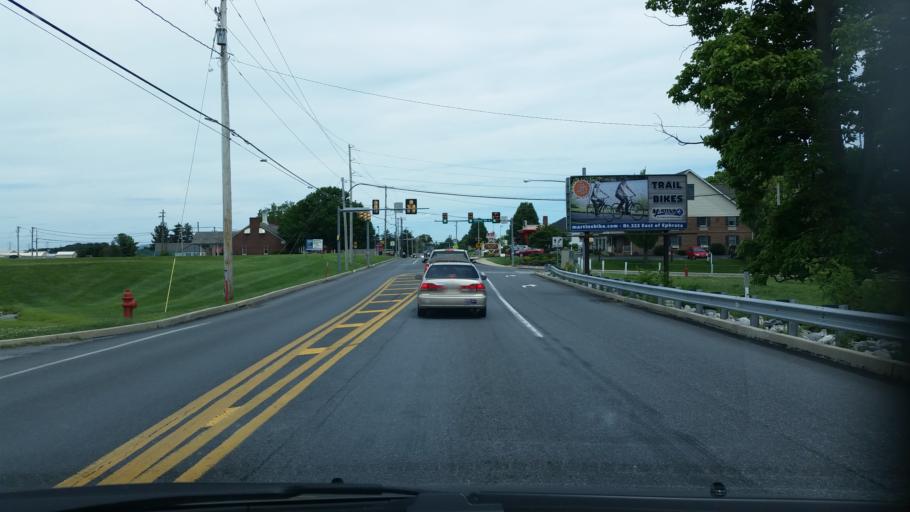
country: US
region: Pennsylvania
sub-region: Lancaster County
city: Lampeter
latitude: 40.0396
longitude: -76.2111
